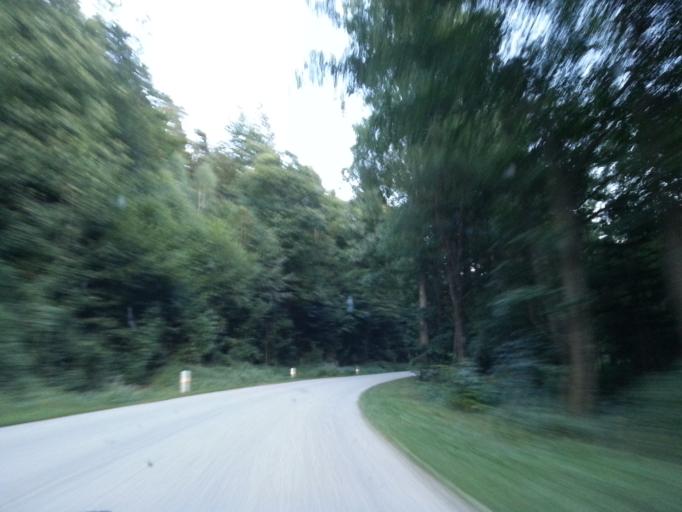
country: FR
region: Alsace
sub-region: Departement du Bas-Rhin
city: Lembach
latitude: 49.0135
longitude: 7.7830
